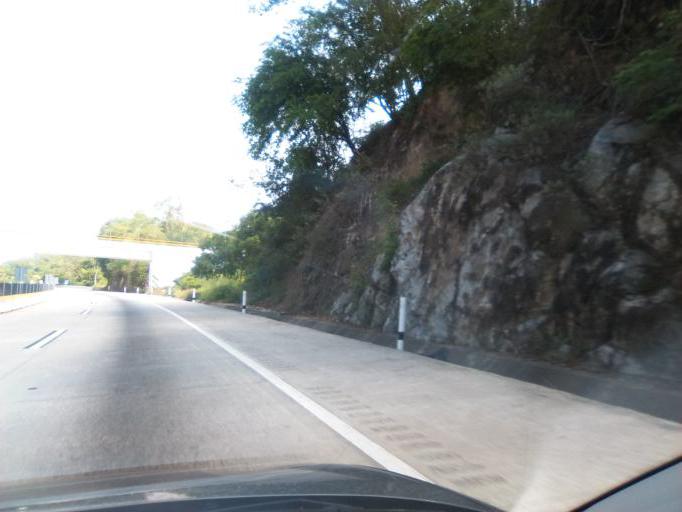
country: MX
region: Guerrero
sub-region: Acapulco de Juarez
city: Kilometro 30
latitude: 16.9516
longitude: -99.7535
